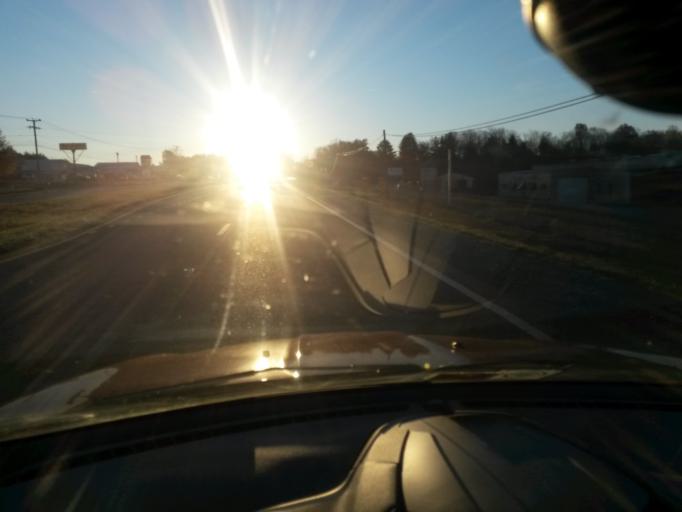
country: US
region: Virginia
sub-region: Franklin County
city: Rocky Mount
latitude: 37.0684
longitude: -79.8914
